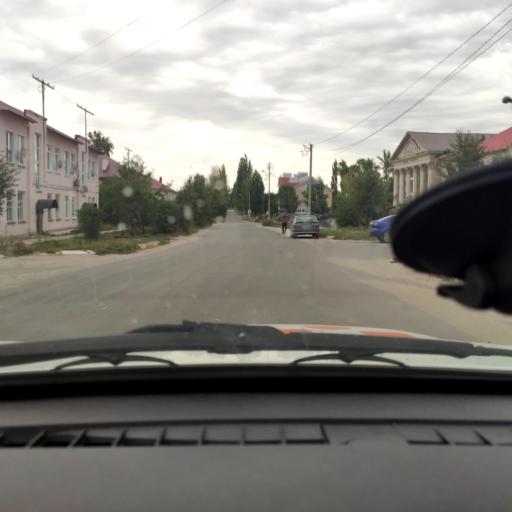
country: RU
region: Voronezj
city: Strelitsa
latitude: 51.6110
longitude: 38.9027
